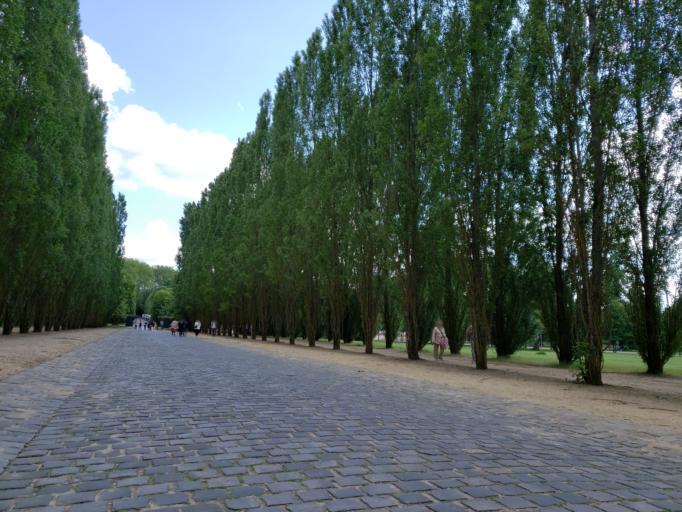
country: FR
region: Ile-de-France
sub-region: Departement des Yvelines
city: Le Chesnay
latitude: 48.8137
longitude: 2.1107
